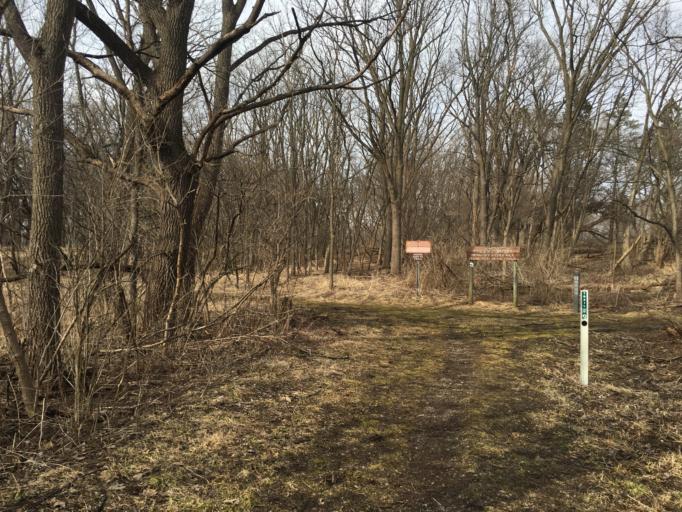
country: US
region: Illinois
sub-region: Cook County
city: Streamwood
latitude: 42.0475
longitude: -88.1983
